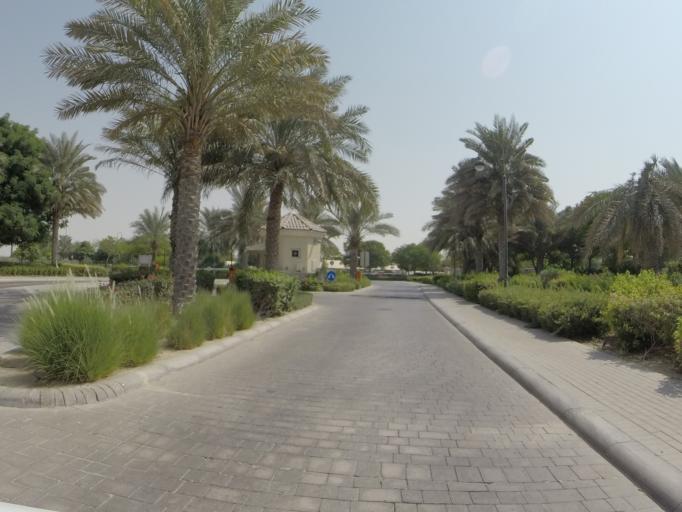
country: AE
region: Dubai
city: Dubai
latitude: 25.0322
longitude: 55.2190
